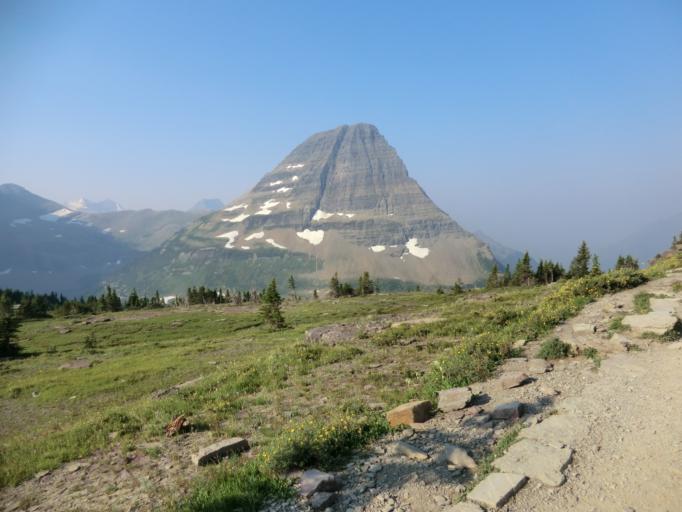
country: US
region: Montana
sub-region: Flathead County
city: Columbia Falls
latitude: 48.6874
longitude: -113.7402
